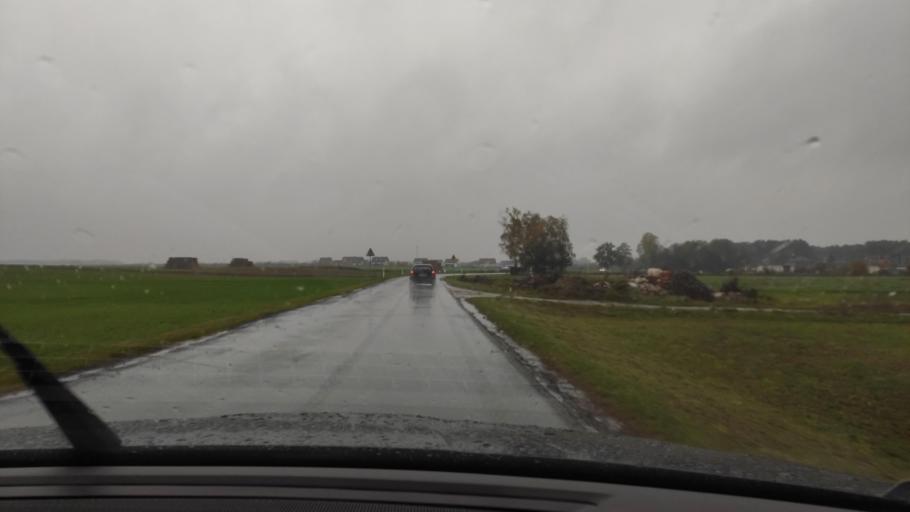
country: PL
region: Greater Poland Voivodeship
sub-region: Powiat poznanski
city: Kornik
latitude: 52.2120
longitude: 17.1001
